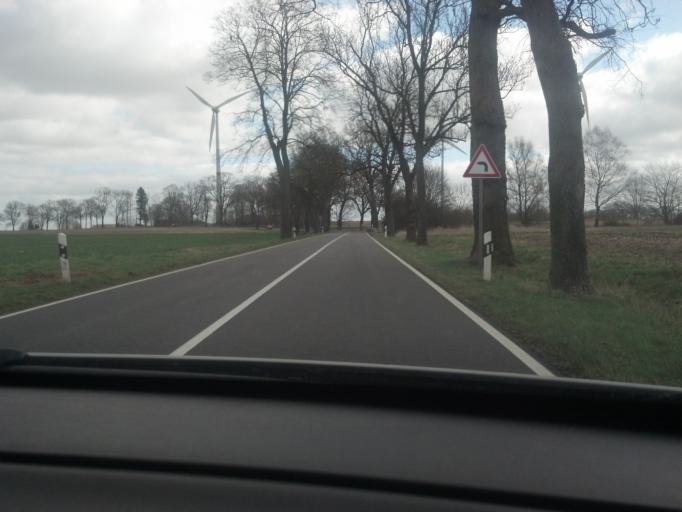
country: DE
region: Brandenburg
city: Gerdshagen
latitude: 53.2986
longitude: 12.2083
